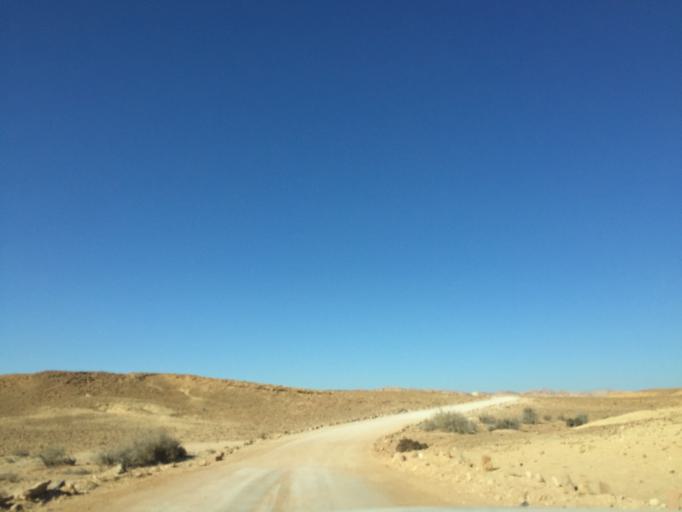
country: IL
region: Southern District
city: Mitzpe Ramon
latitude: 30.6176
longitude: 34.9307
